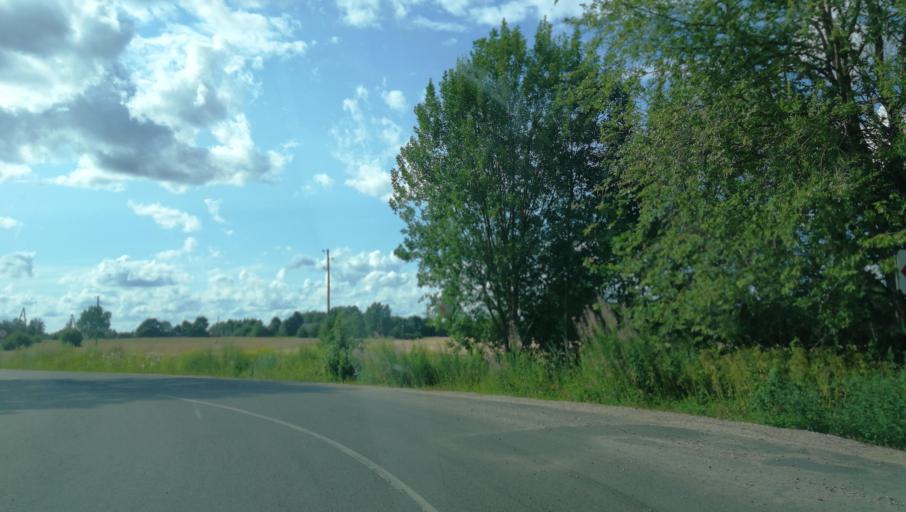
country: LV
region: Cesu Rajons
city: Cesis
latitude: 57.3225
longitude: 25.3094
